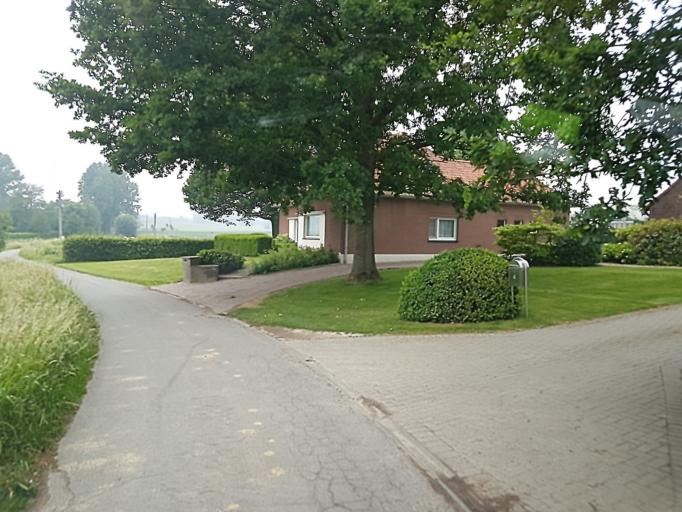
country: BE
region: Flanders
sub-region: Provincie West-Vlaanderen
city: Anzegem
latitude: 50.8278
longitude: 3.4842
